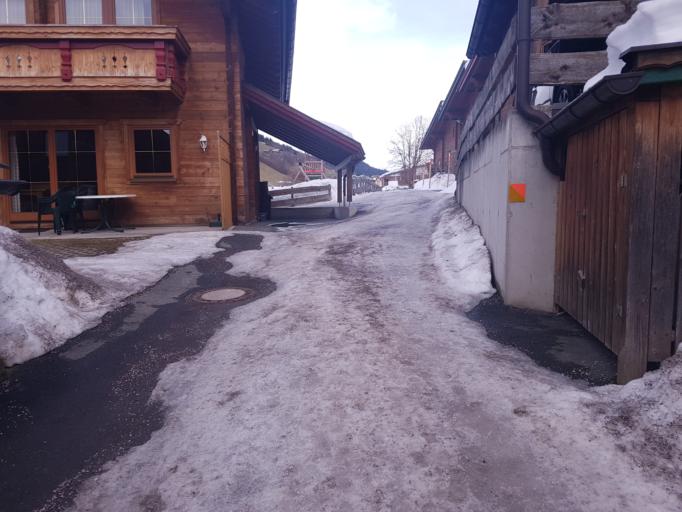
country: AT
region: Tyrol
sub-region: Politischer Bezirk Kufstein
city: Worgl
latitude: 47.4504
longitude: 12.0892
